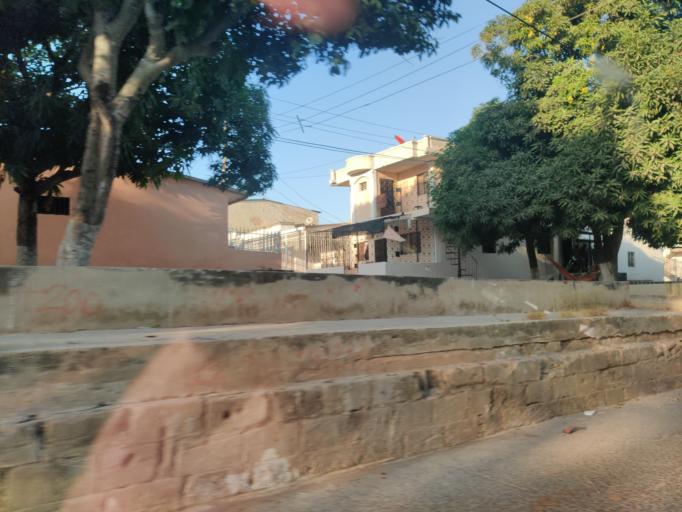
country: CO
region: Atlantico
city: Soledad
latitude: 10.9200
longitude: -74.8006
